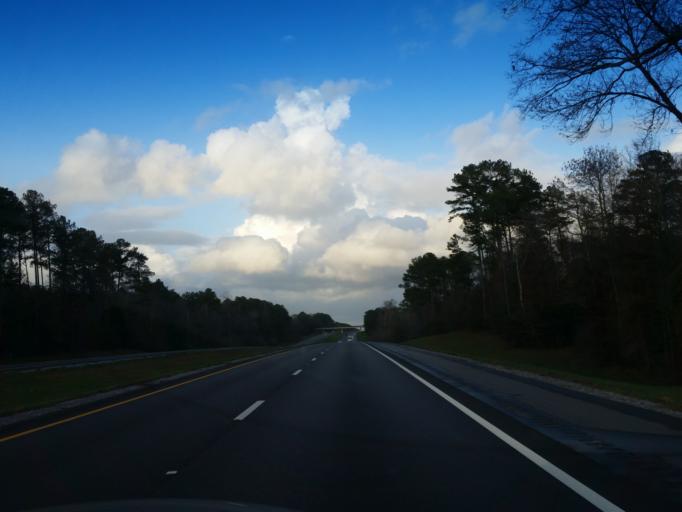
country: US
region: Mississippi
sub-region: Jones County
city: Sharon
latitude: 31.8787
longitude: -89.0421
